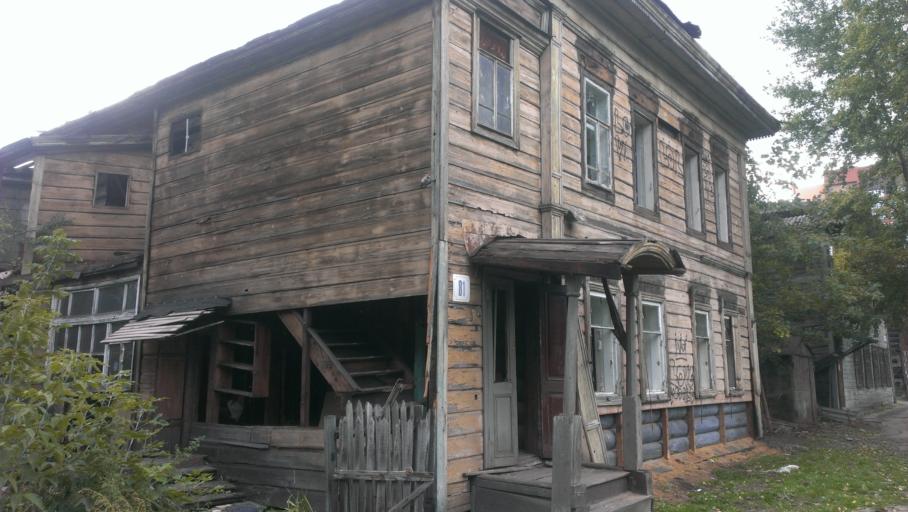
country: RU
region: Altai Krai
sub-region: Gorod Barnaulskiy
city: Barnaul
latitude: 53.3361
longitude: 83.7836
